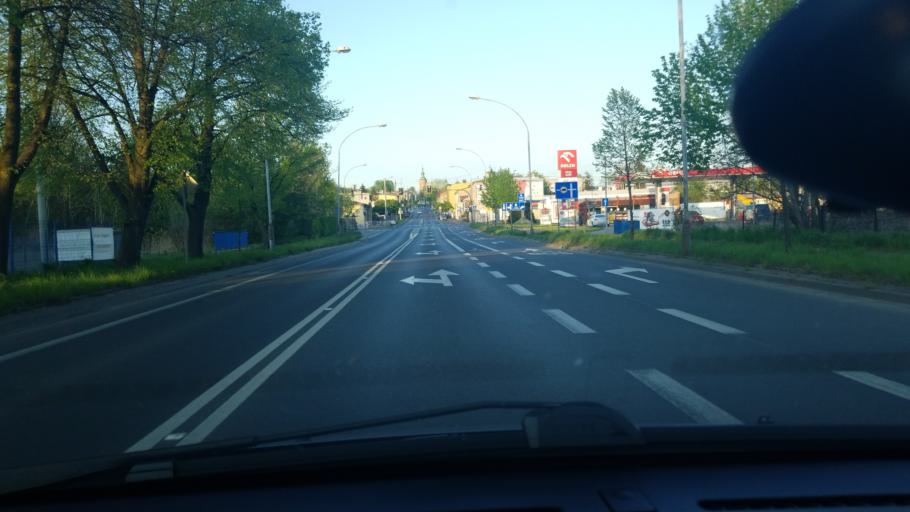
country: PL
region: Silesian Voivodeship
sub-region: Czestochowa
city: Czestochowa
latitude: 50.8030
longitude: 19.0859
